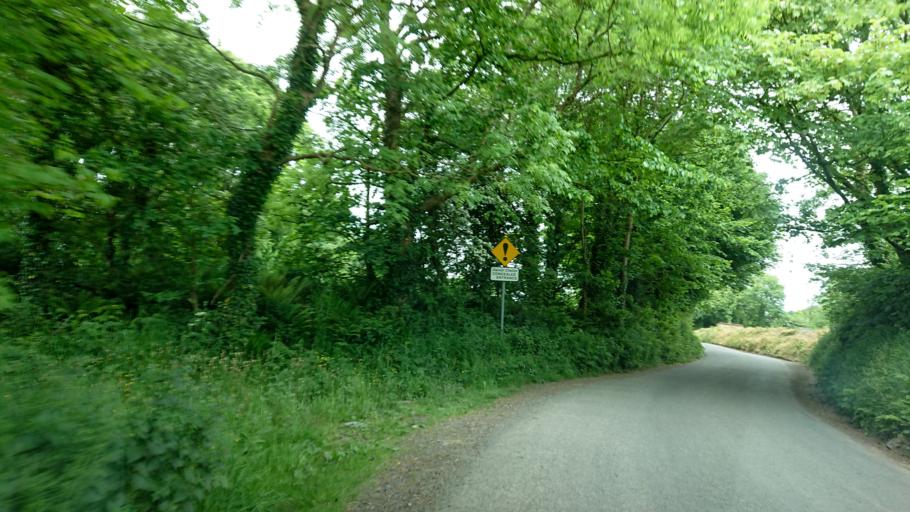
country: IE
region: Munster
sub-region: Waterford
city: Waterford
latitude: 52.2289
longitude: -7.0327
